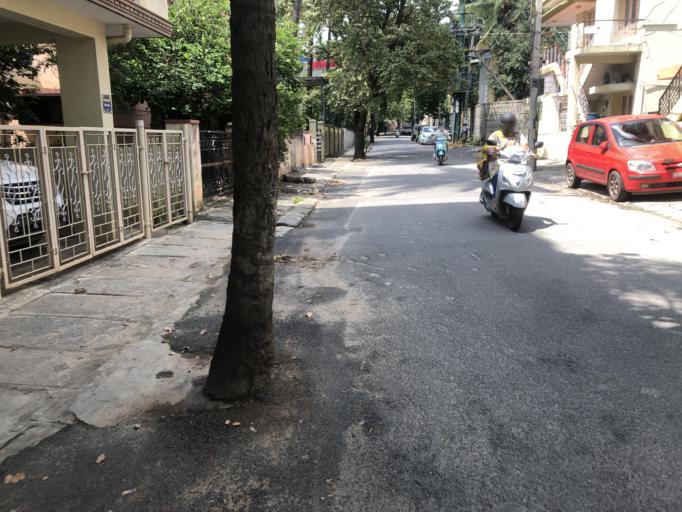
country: IN
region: Karnataka
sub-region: Bangalore Urban
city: Bangalore
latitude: 12.9367
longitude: 77.5491
